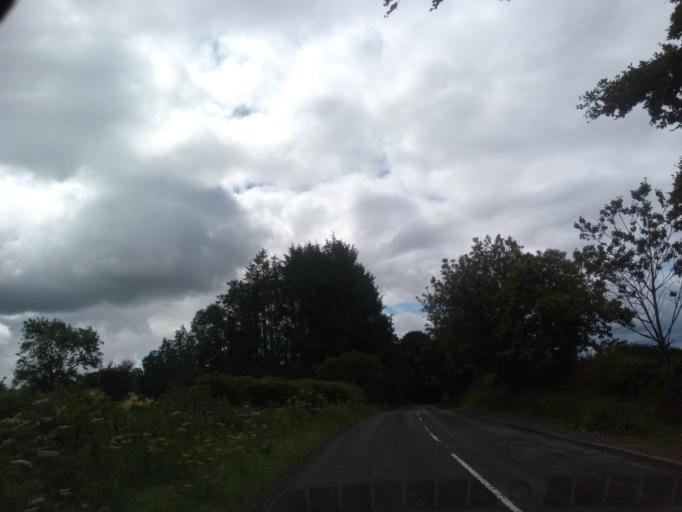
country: GB
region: Scotland
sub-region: Stirling
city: Doune
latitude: 56.1861
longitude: -4.0192
